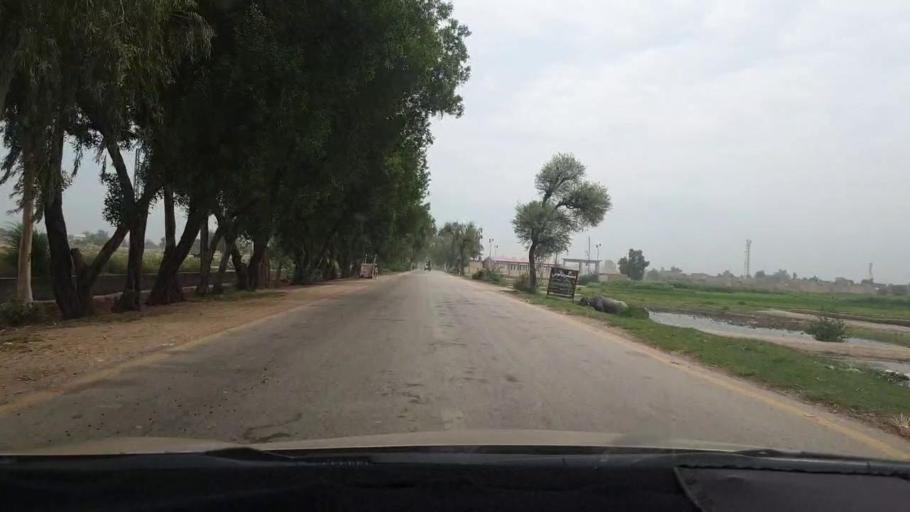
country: PK
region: Sindh
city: Naudero
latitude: 27.6668
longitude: 68.3502
